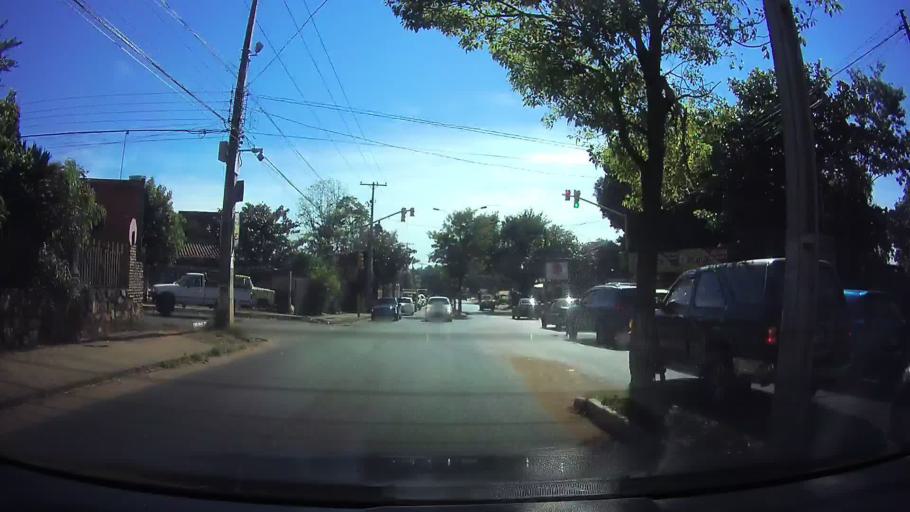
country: PY
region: Central
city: Villa Elisa
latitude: -25.3675
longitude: -57.5785
